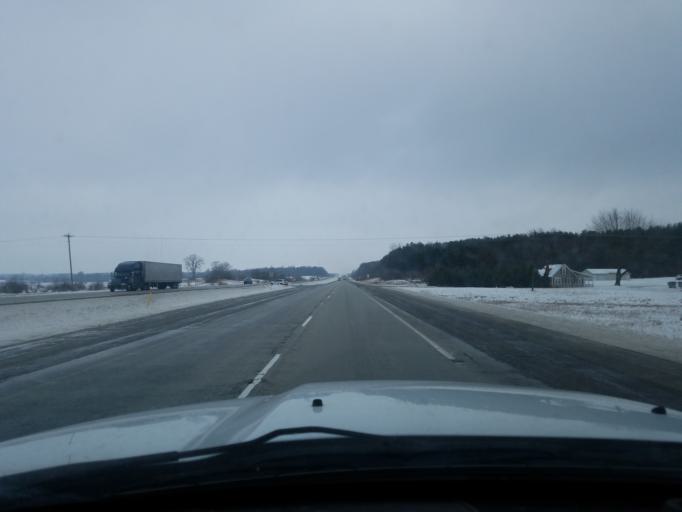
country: US
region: Indiana
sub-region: Fulton County
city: Rochester
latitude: 41.1195
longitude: -86.2397
